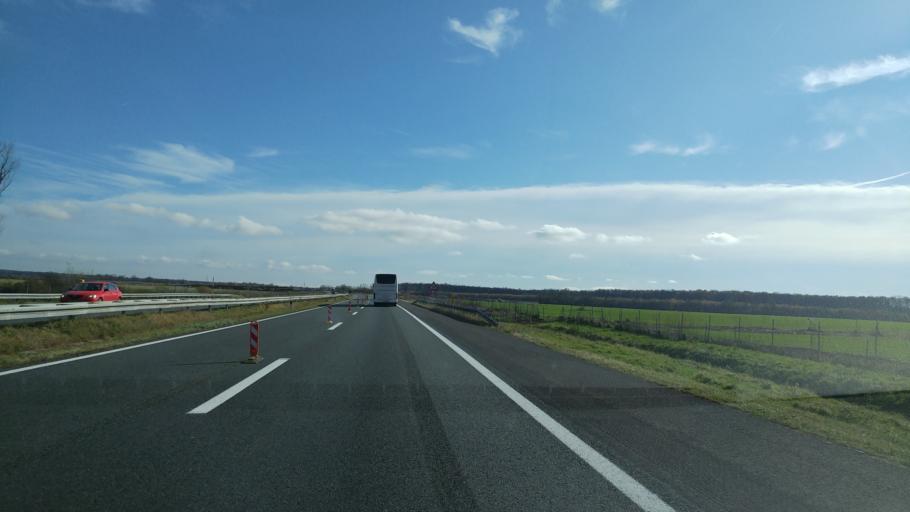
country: HR
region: Sisacko-Moslavacka
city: Lipovljani
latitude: 45.3768
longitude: 16.8771
